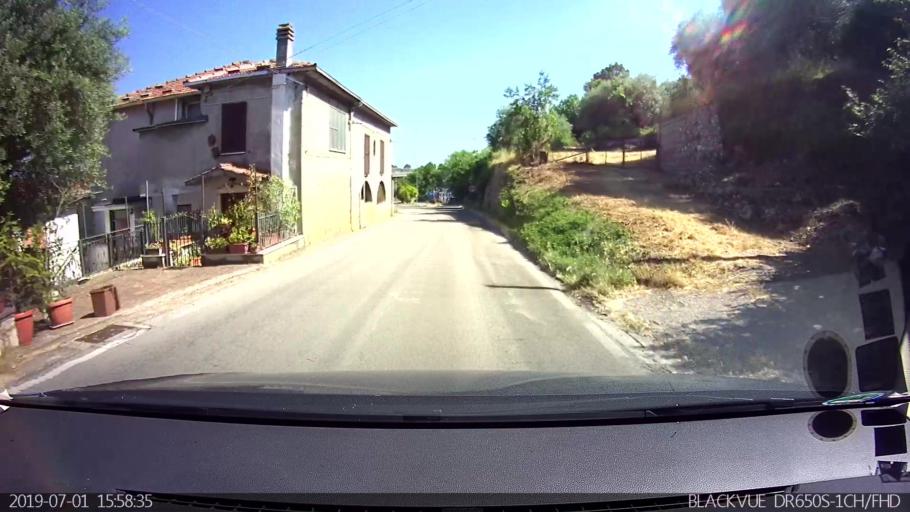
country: IT
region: Latium
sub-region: Provincia di Frosinone
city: Sant'Angelo in Villa-Giglio
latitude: 41.6665
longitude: 13.4237
